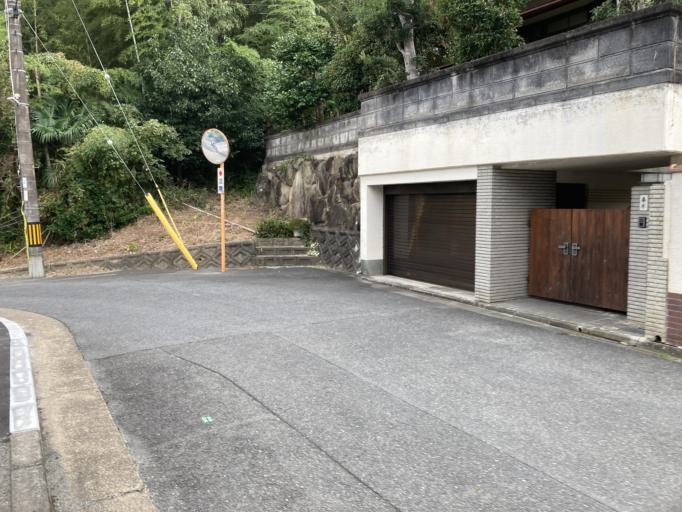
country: JP
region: Nara
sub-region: Ikoma-shi
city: Ikoma
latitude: 34.6834
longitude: 135.6982
